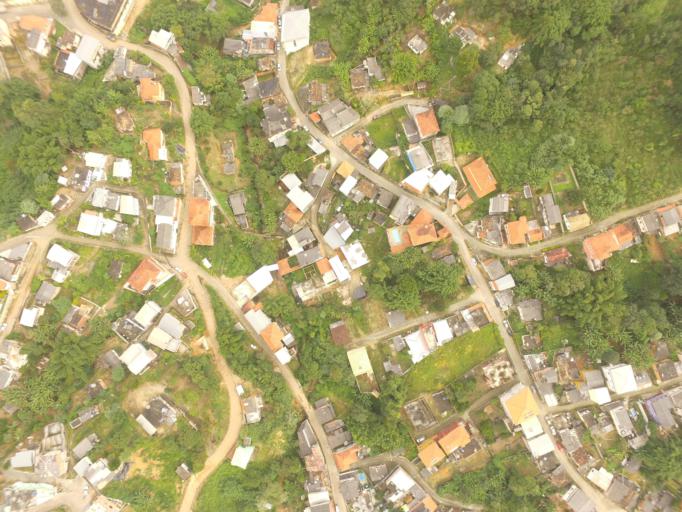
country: BR
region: Minas Gerais
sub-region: Tiradentes
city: Tiradentes
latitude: -21.0543
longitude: -44.0759
